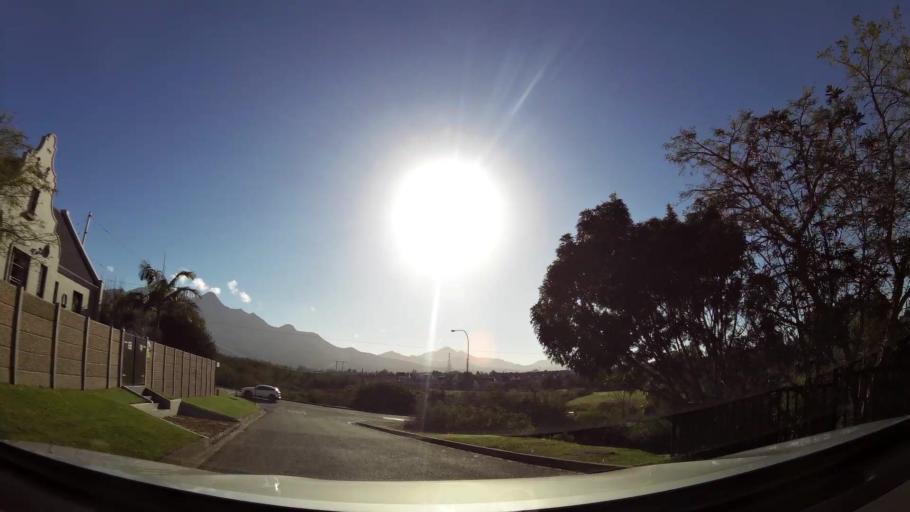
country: ZA
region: Western Cape
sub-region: Eden District Municipality
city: George
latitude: -33.9696
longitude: 22.4417
